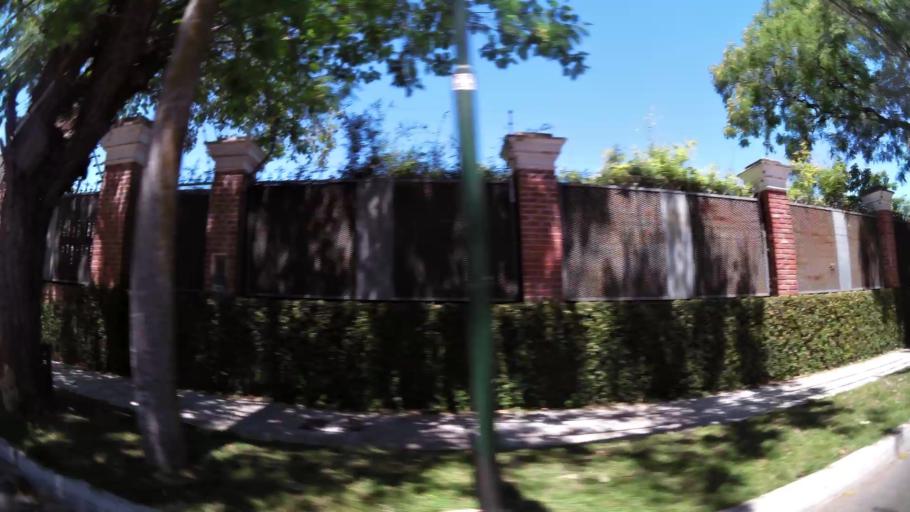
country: AR
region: Buenos Aires
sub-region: Partido de San Isidro
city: San Isidro
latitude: -34.4538
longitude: -58.5240
